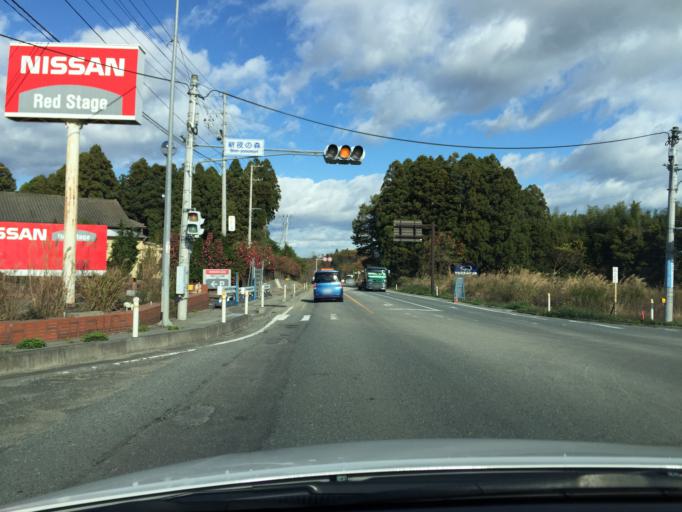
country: JP
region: Fukushima
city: Namie
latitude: 37.3654
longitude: 141.0092
